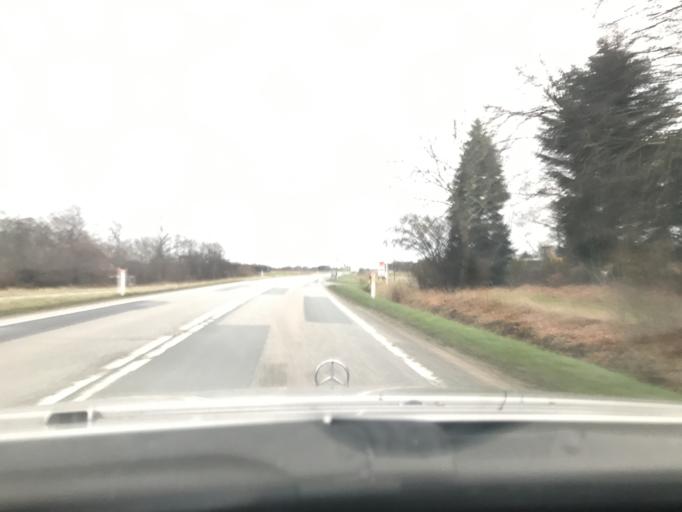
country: DK
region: South Denmark
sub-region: Tonder Kommune
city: Toftlund
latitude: 55.1317
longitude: 9.1386
